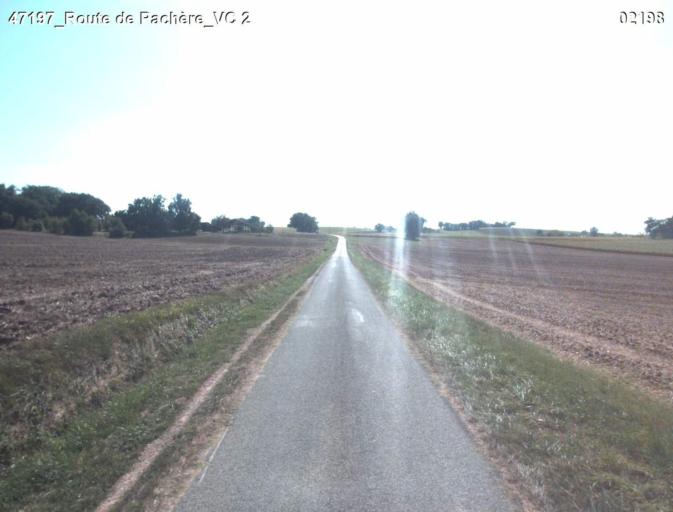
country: FR
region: Aquitaine
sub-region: Departement du Lot-et-Garonne
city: Laplume
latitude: 44.0865
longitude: 0.4488
